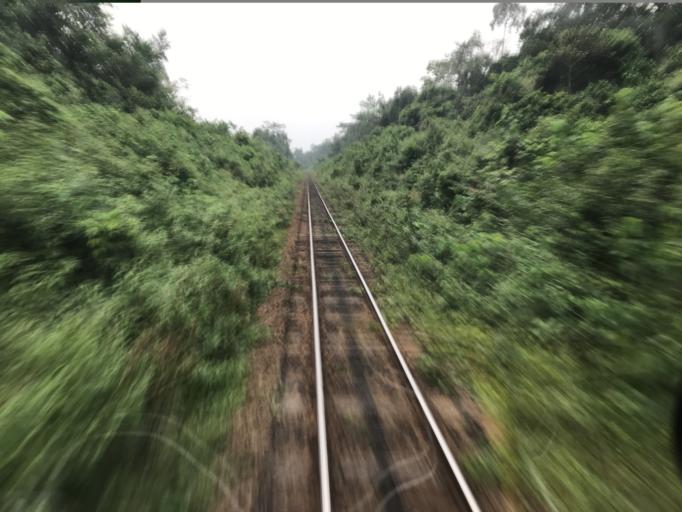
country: CM
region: Littoral
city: Edea
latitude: 3.9601
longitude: 10.0844
